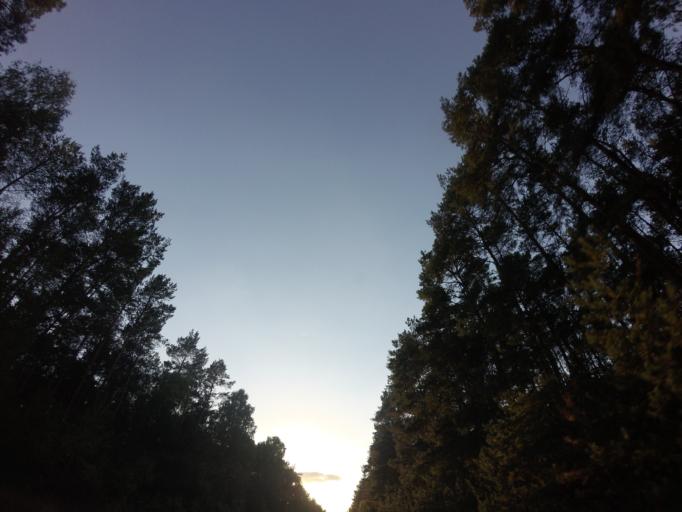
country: PL
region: Greater Poland Voivodeship
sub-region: Powiat miedzychodzki
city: Miedzychod
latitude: 52.5021
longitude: 15.9417
